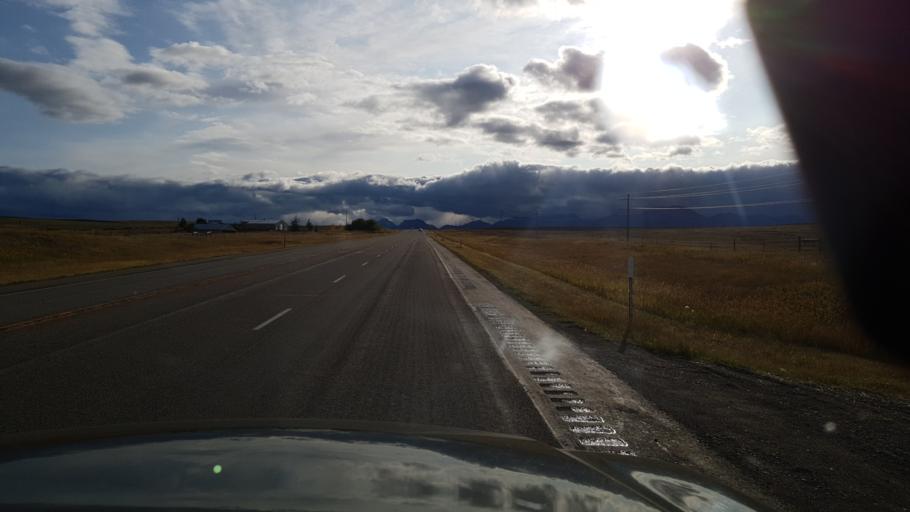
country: US
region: Montana
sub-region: Glacier County
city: South Browning
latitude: 48.5108
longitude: -113.0942
